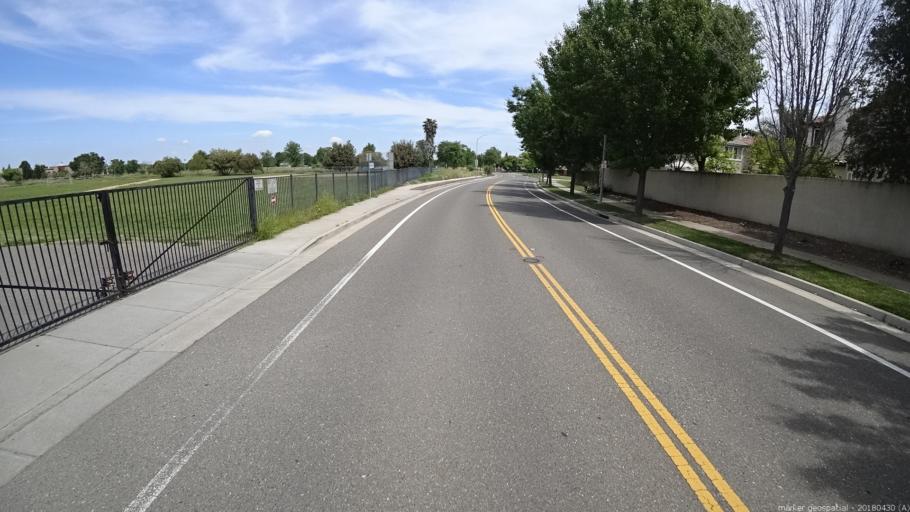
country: US
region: California
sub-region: Yolo County
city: West Sacramento
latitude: 38.5489
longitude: -121.5330
